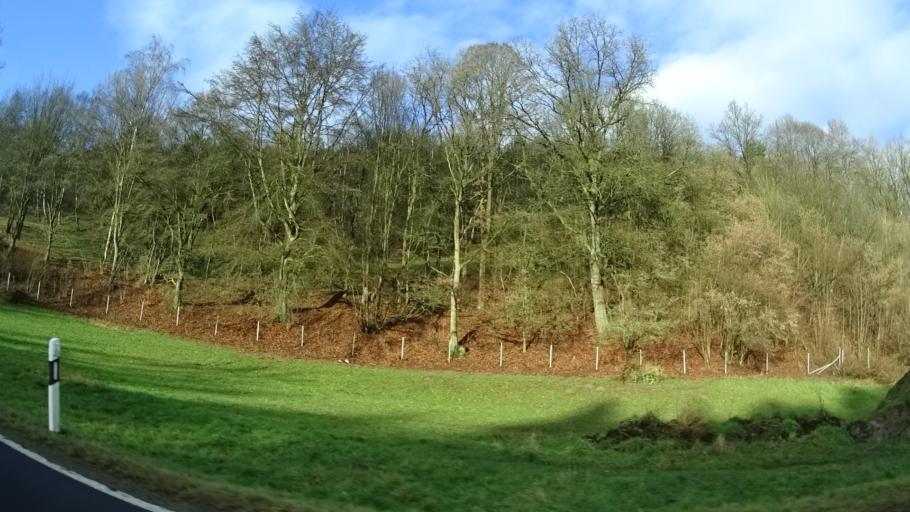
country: DE
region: Thuringia
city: Wernshausen
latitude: 50.7261
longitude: 10.3322
